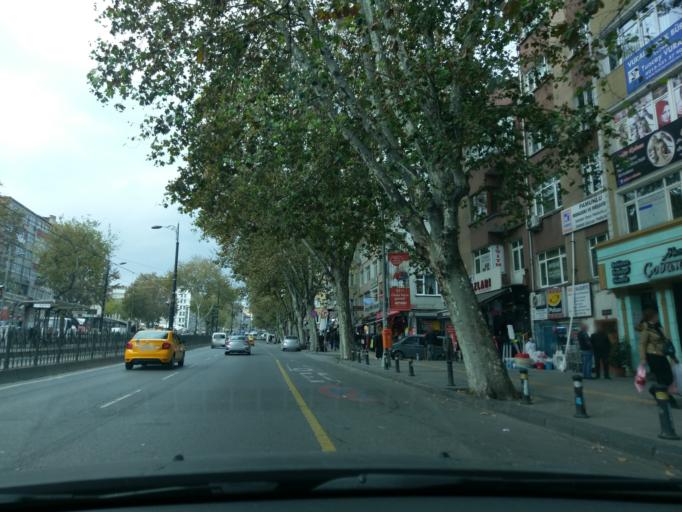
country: TR
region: Istanbul
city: Istanbul
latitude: 41.0111
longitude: 28.9436
